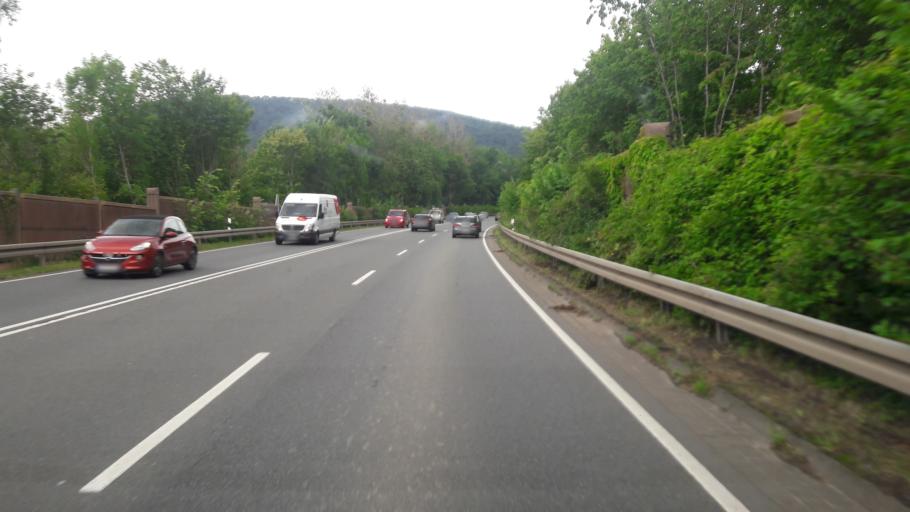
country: DE
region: Lower Saxony
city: Luhden
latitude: 52.2027
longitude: 9.0949
